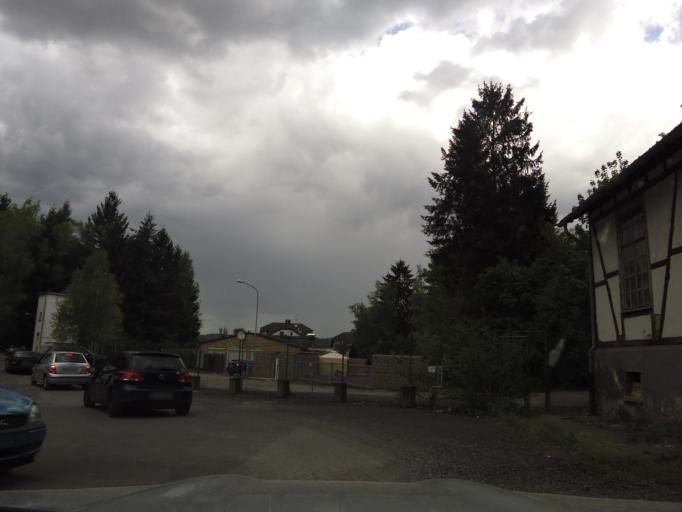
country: DE
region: Hesse
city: Albshausen
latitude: 50.5366
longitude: 8.4385
